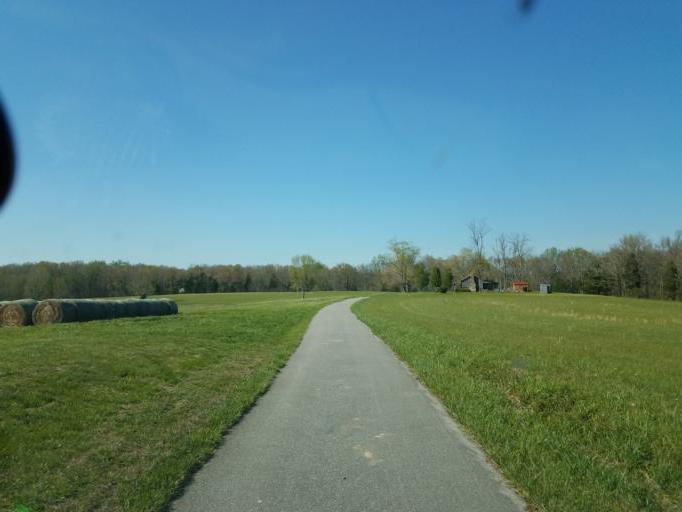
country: US
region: Kentucky
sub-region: Edmonson County
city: Brownsville
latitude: 37.1356
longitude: -86.1471
